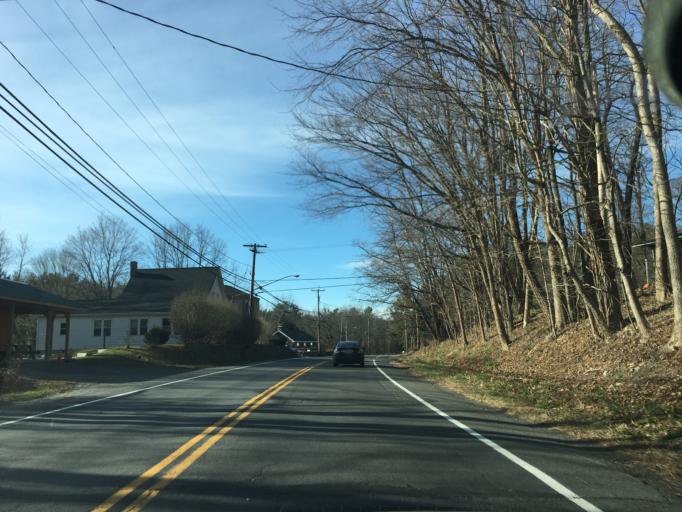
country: US
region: New York
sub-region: Rensselaer County
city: West Sand Lake
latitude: 42.6447
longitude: -73.5869
